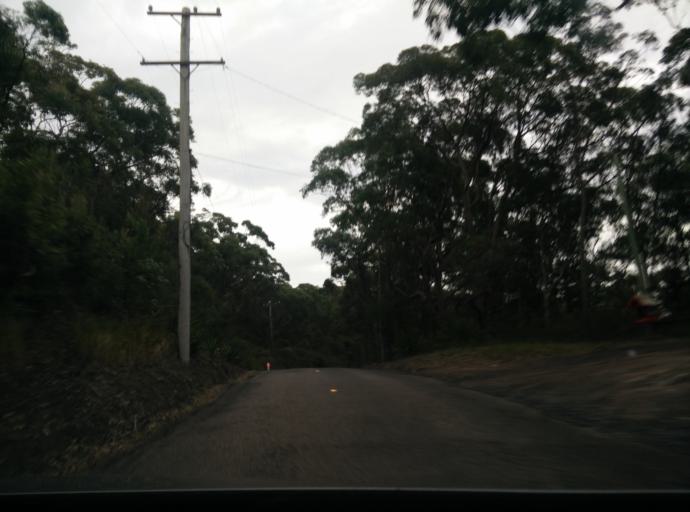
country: AU
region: New South Wales
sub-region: Gosford Shire
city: Narara
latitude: -33.3641
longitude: 151.3095
